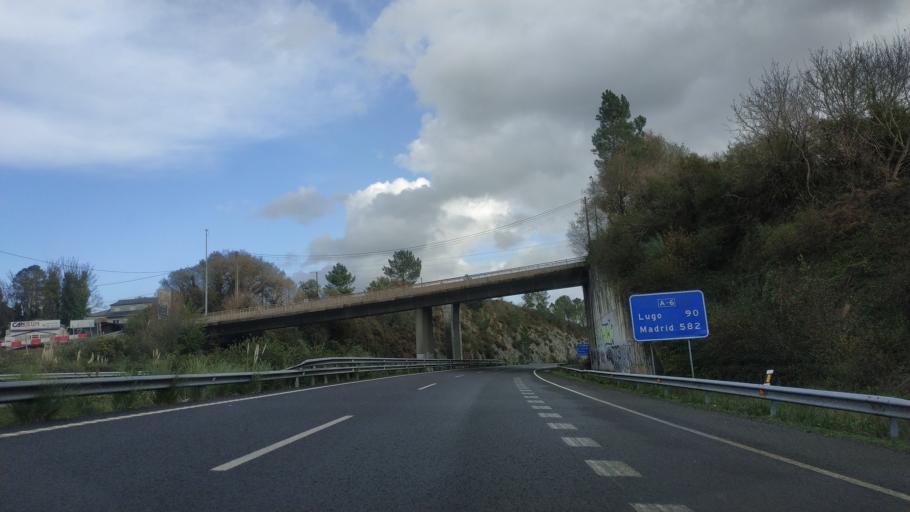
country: ES
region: Galicia
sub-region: Provincia da Coruna
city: Culleredo
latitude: 43.2746
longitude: -8.3655
